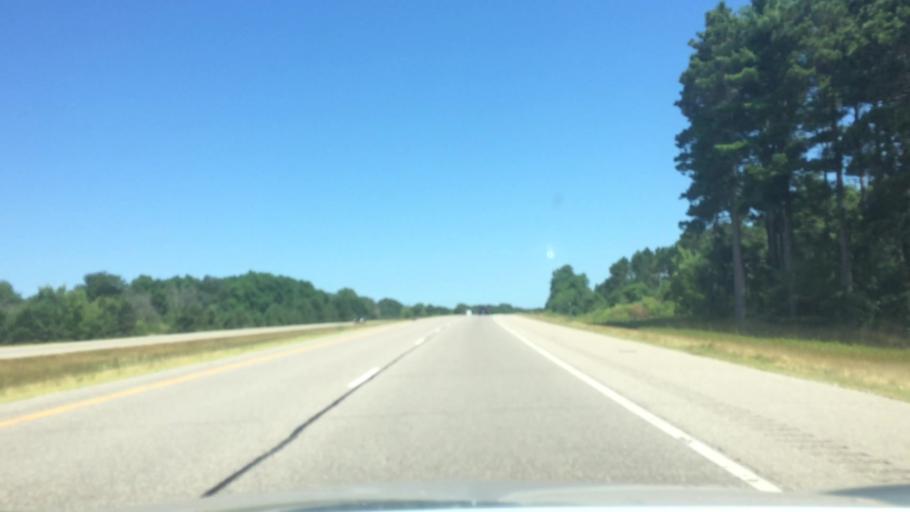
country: US
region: Wisconsin
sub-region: Marquette County
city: Westfield
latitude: 44.0554
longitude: -89.5410
